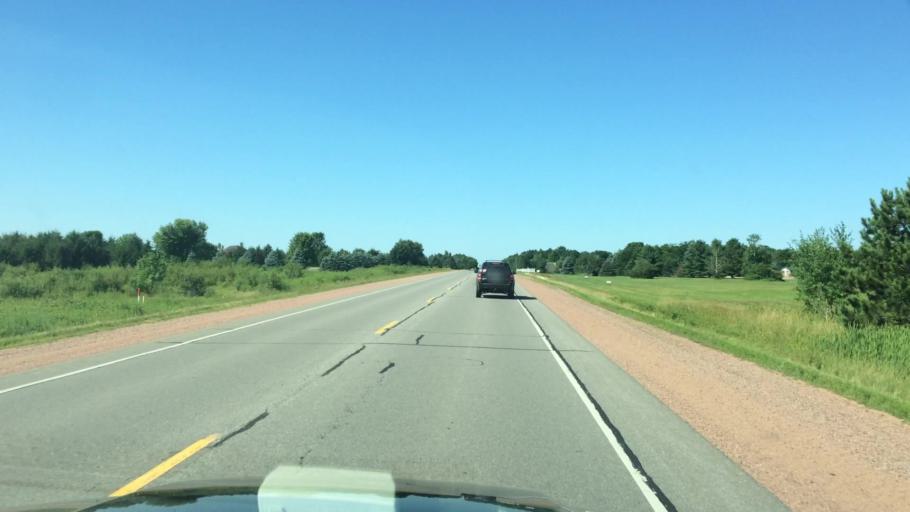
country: US
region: Wisconsin
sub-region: Wood County
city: Marshfield
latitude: 44.7193
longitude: -90.1043
